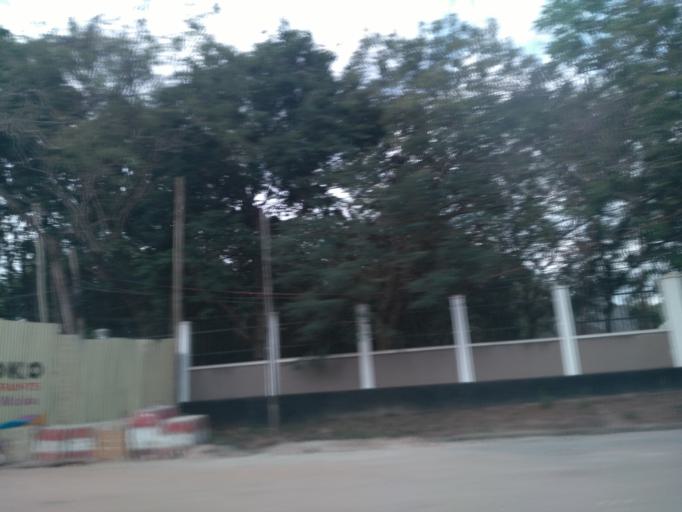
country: TZ
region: Dar es Salaam
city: Magomeni
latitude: -6.7472
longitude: 39.2402
